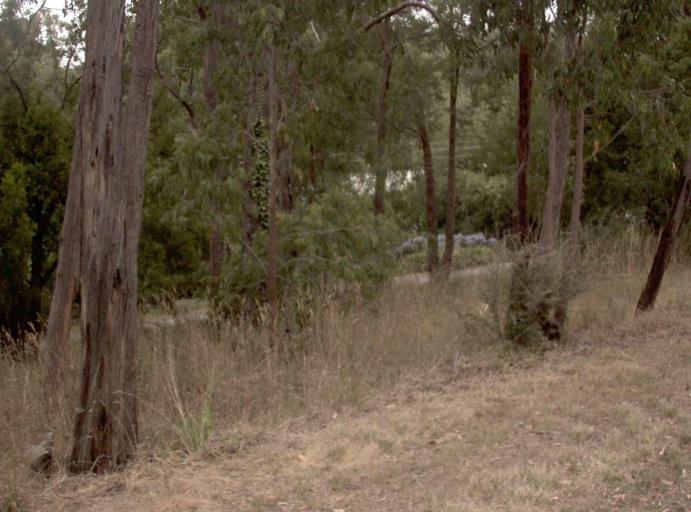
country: AU
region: Victoria
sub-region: Yarra Ranges
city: Badger Creek
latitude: -37.6896
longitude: 145.5472
